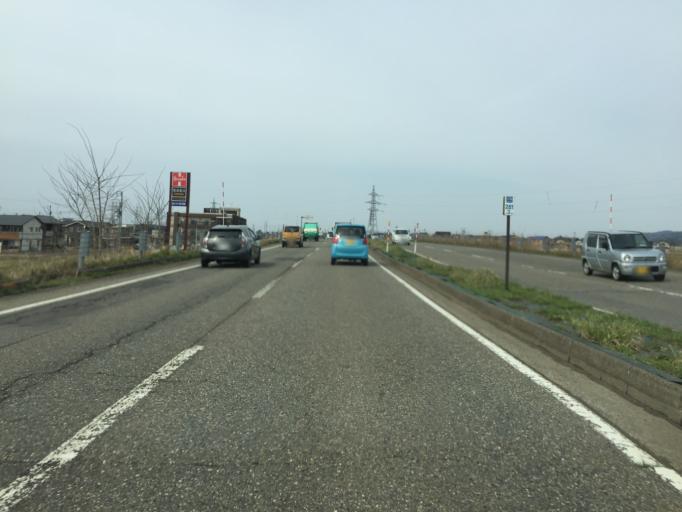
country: JP
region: Niigata
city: Nagaoka
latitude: 37.4283
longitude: 138.8650
